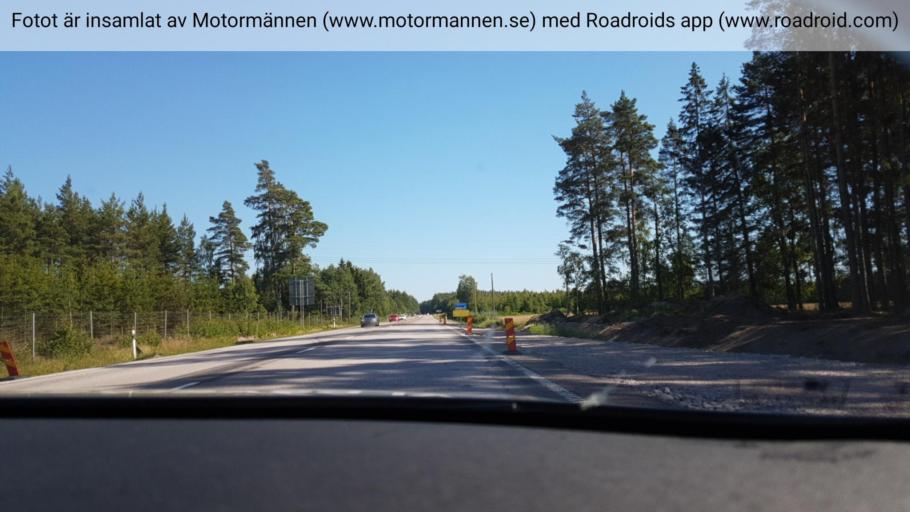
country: SE
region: Vaestra Goetaland
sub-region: Lidkopings Kommun
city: Lidkoping
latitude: 58.4788
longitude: 13.2025
